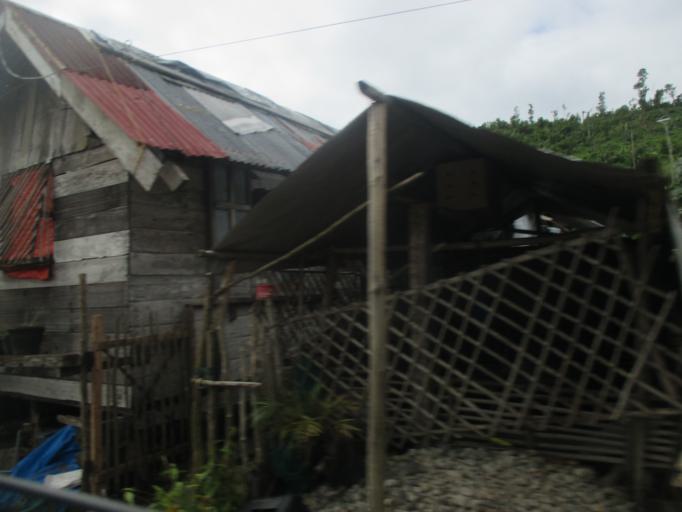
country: PH
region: Eastern Visayas
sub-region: Province of Eastern Samar
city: Lawa-an
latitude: 11.1068
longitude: 125.2111
